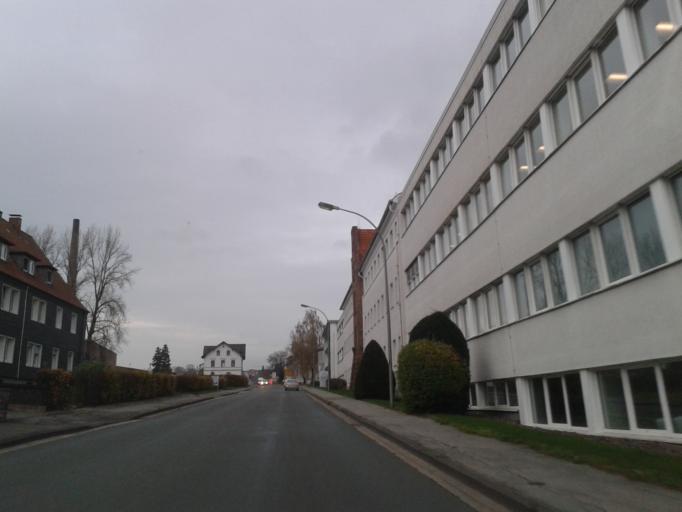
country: DE
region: North Rhine-Westphalia
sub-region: Regierungsbezirk Detmold
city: Blomberg
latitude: 51.9344
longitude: 9.1004
